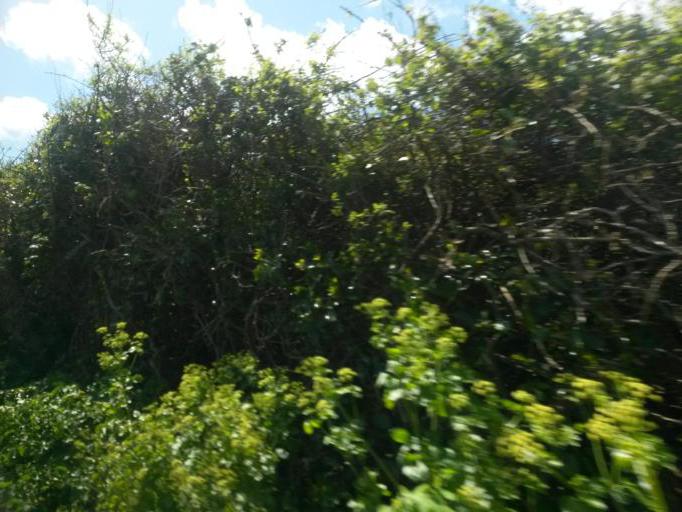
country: IE
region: Munster
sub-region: Waterford
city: Dunmore East
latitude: 52.1764
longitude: -6.8955
